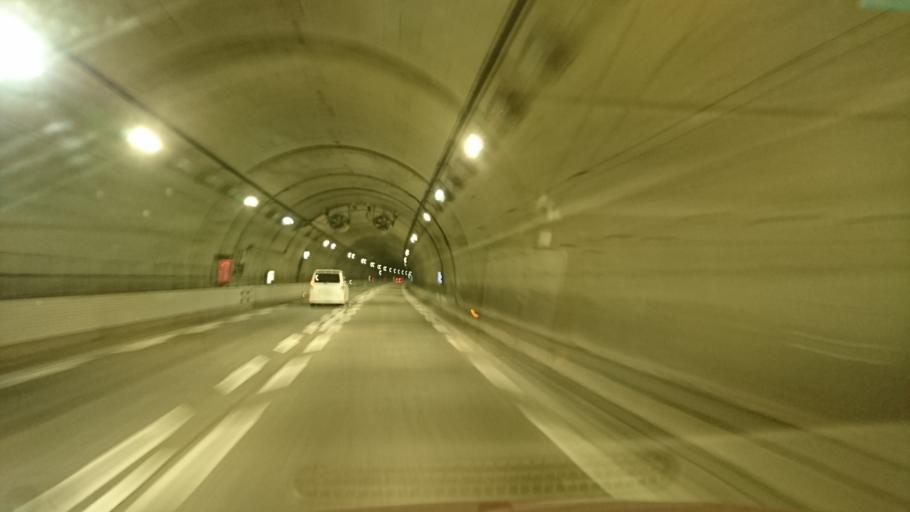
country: JP
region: Okayama
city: Soja
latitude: 34.6412
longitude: 133.8078
